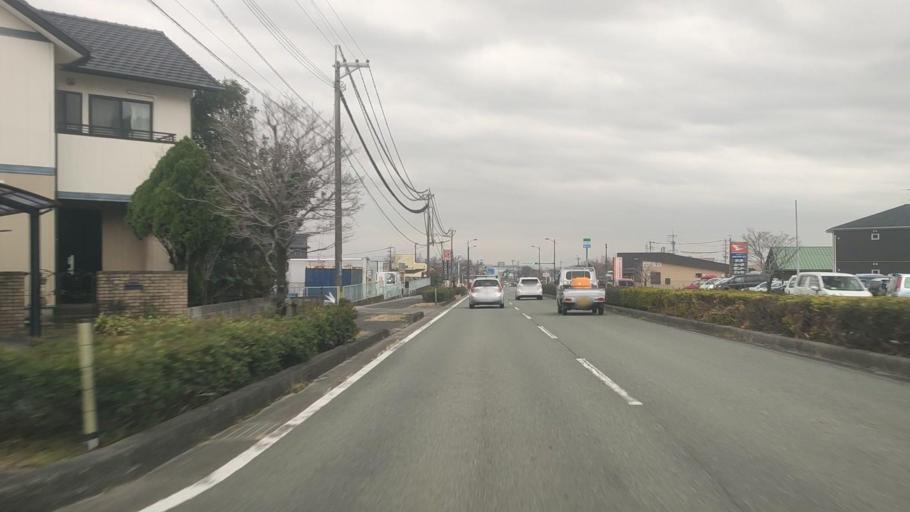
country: JP
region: Kumamoto
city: Ozu
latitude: 32.8323
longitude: 130.7994
